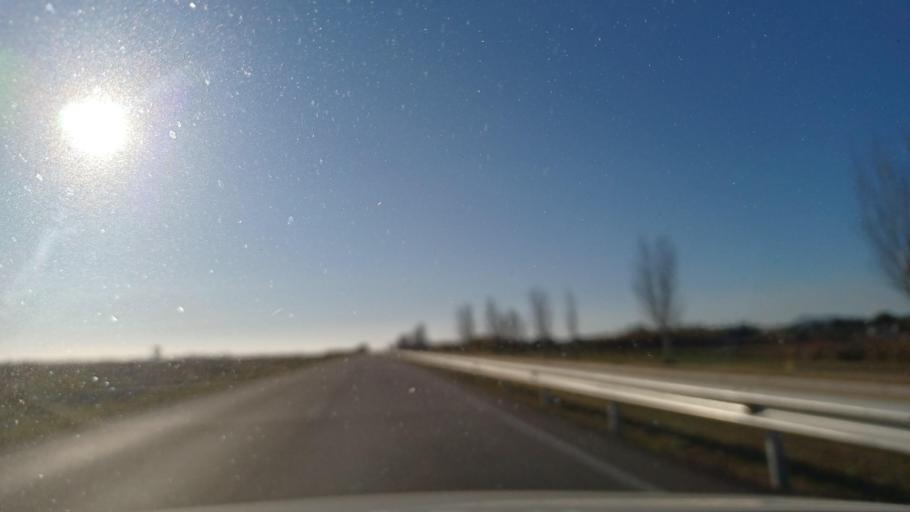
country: ES
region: Catalonia
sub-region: Provincia de Tarragona
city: Sant Carles de la Rapita
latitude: 40.6536
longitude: 0.5953
